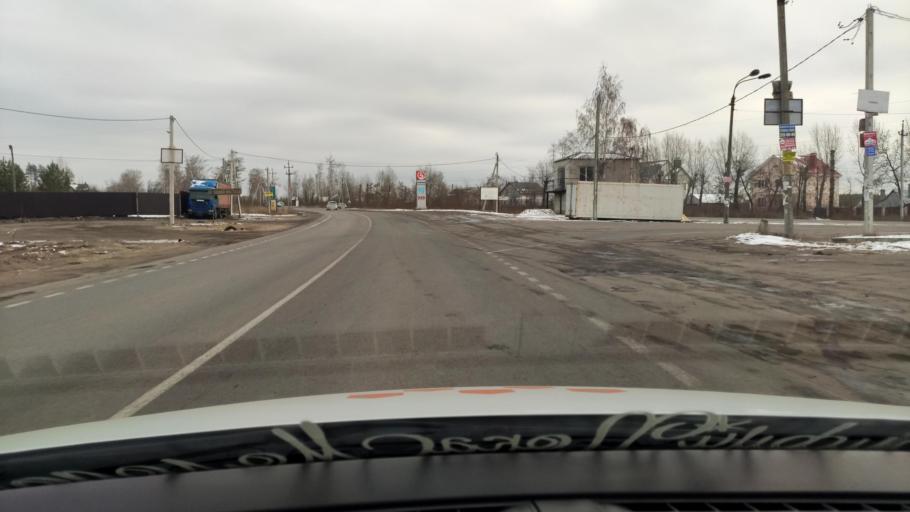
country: RU
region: Voronezj
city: Ramon'
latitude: 51.8913
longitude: 39.1813
